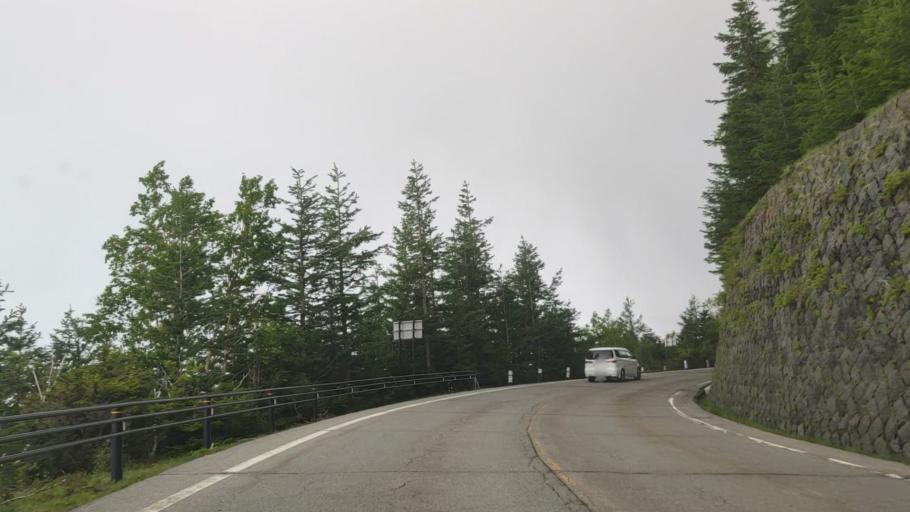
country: JP
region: Yamanashi
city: Fujikawaguchiko
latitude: 35.3836
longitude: 138.6977
